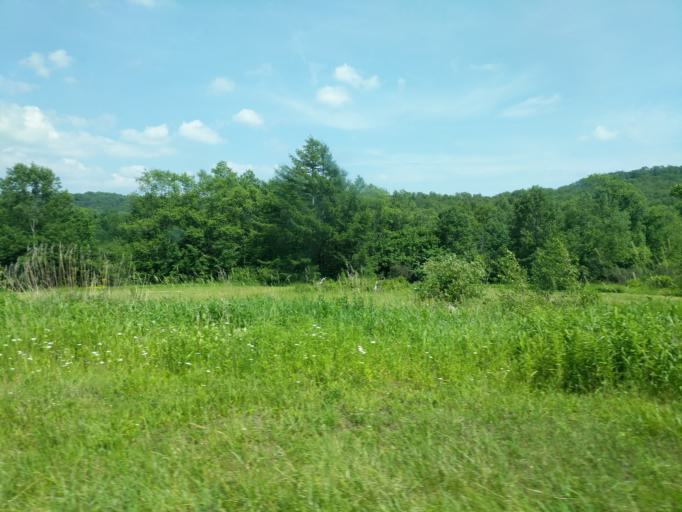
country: US
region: New York
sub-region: Sullivan County
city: Livingston Manor
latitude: 41.9078
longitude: -74.9432
